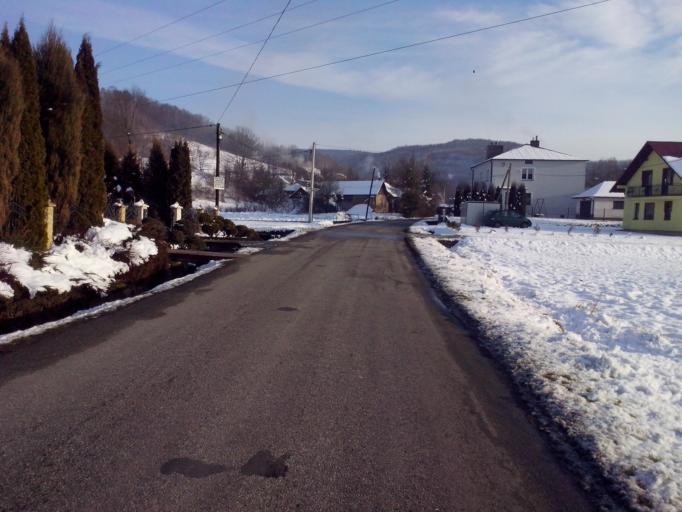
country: PL
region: Subcarpathian Voivodeship
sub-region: Powiat strzyzowski
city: Strzyzow
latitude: 49.8651
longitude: 21.8269
